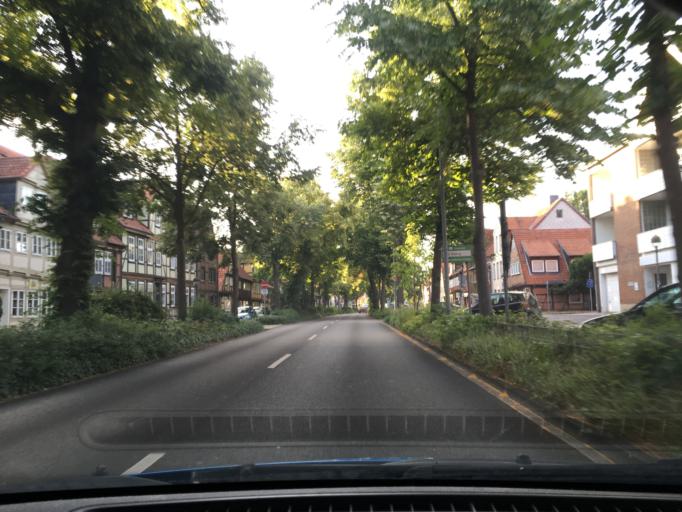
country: DE
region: Lower Saxony
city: Celle
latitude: 52.6203
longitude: 10.0910
